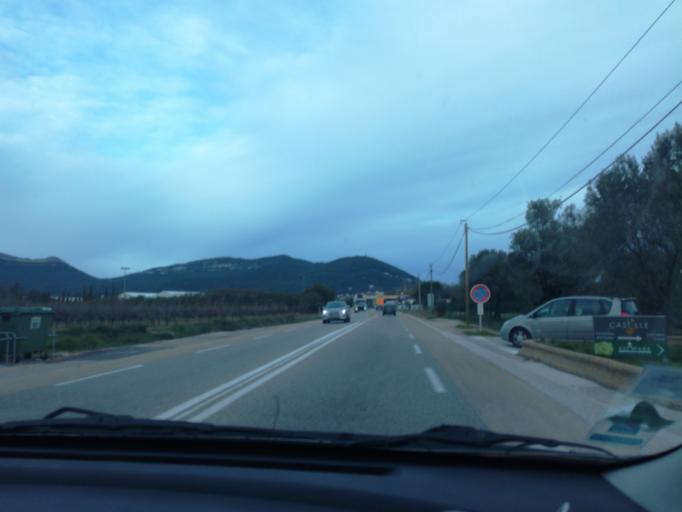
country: FR
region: Provence-Alpes-Cote d'Azur
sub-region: Departement du Var
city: La Crau
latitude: 43.1579
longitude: 6.0660
